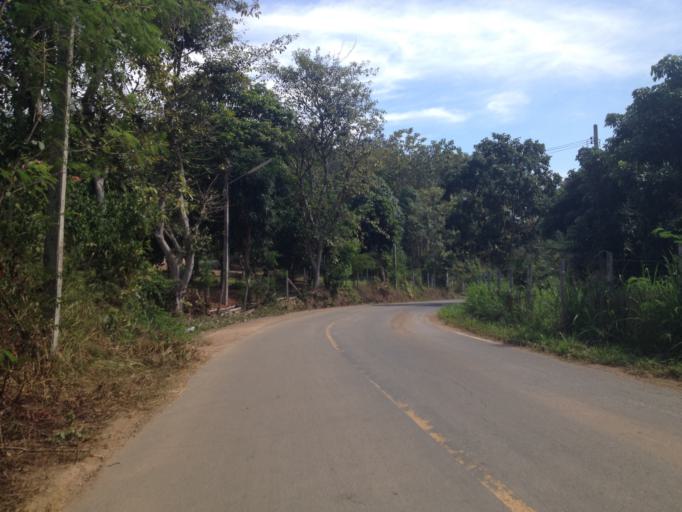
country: TH
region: Chiang Mai
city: Hang Dong
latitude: 18.7165
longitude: 98.8897
